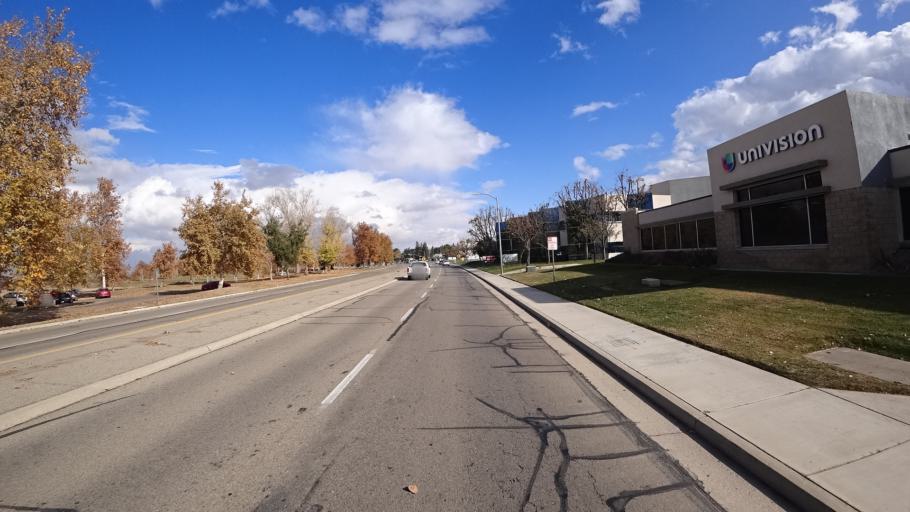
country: US
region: California
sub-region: Kern County
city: Greenacres
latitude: 35.3638
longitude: -119.0685
